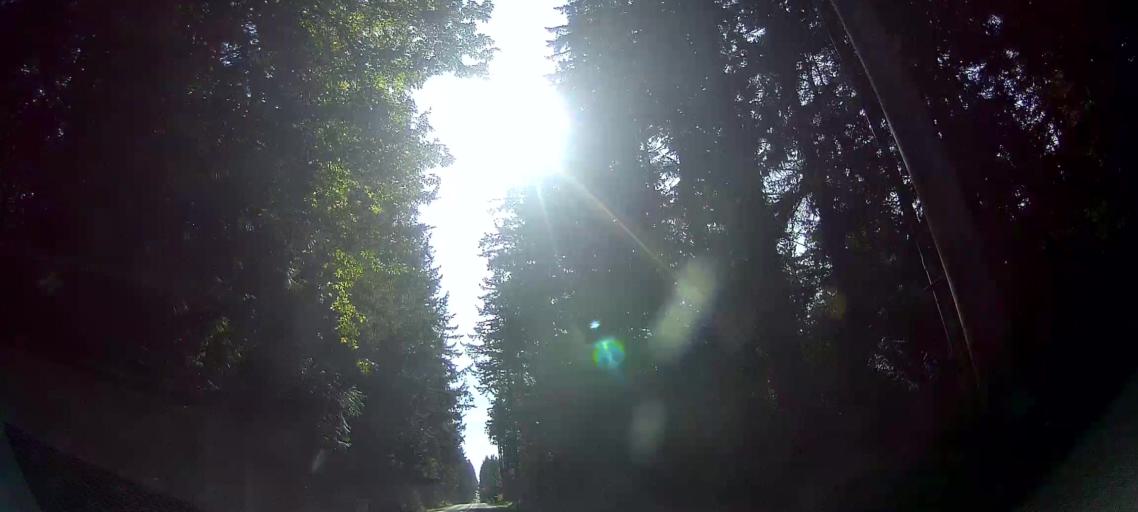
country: US
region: Washington
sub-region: Island County
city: Camano
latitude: 48.2209
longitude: -122.4559
